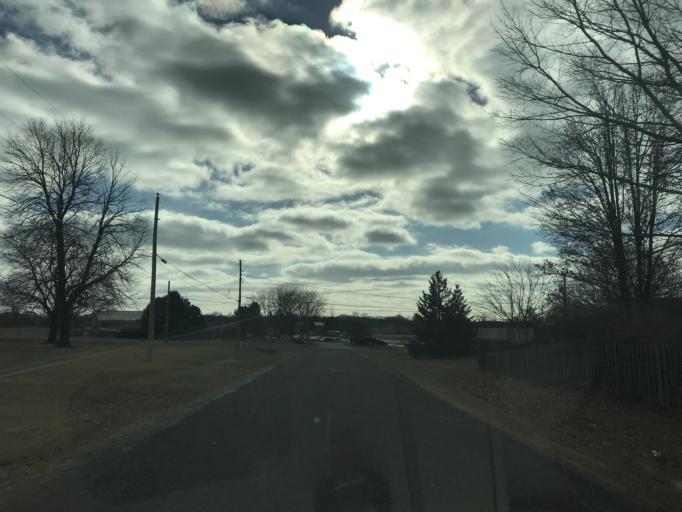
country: US
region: Wisconsin
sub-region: Dane County
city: Monona
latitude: 43.1076
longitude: -89.2900
